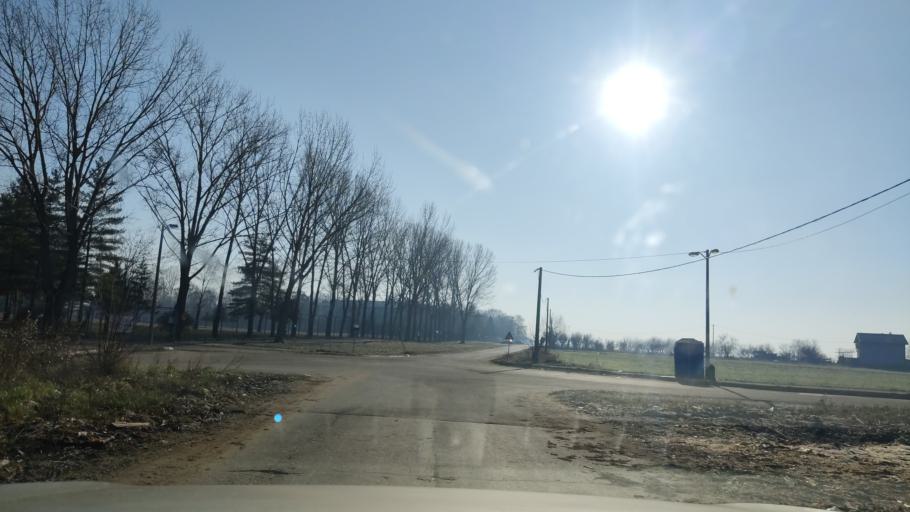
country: RS
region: Central Serbia
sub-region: Belgrade
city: Surcin
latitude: 44.7456
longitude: 20.2709
